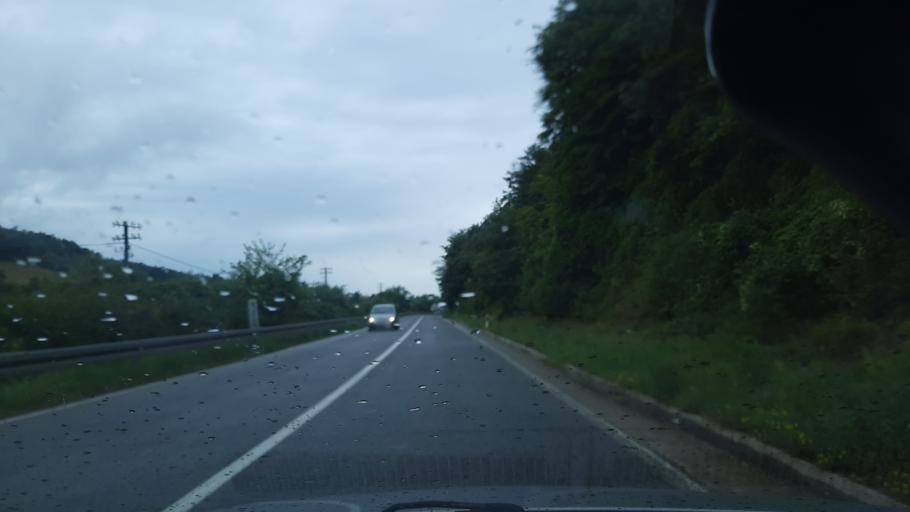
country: RS
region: Central Serbia
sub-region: Sumadijski Okrug
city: Knic
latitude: 43.8491
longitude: 20.7716
